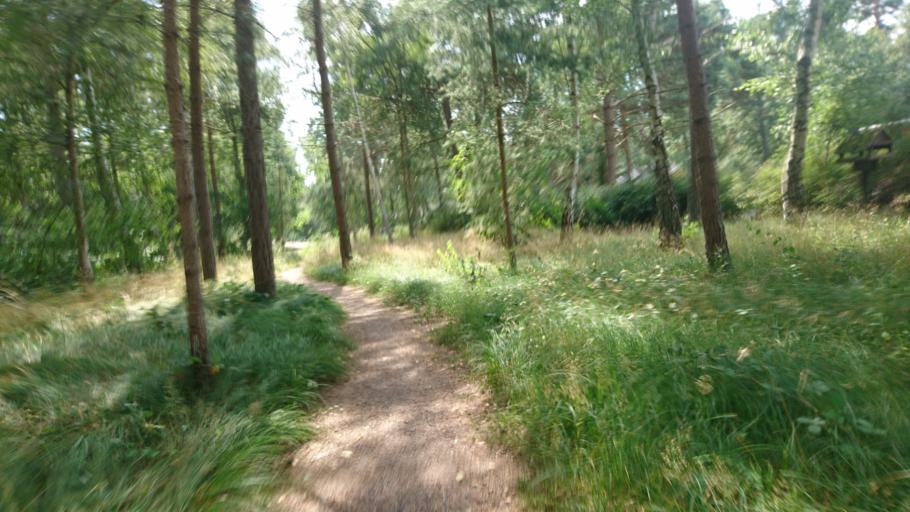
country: SE
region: Skane
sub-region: Vellinge Kommun
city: Ljunghusen
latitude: 55.4041
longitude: 12.9146
